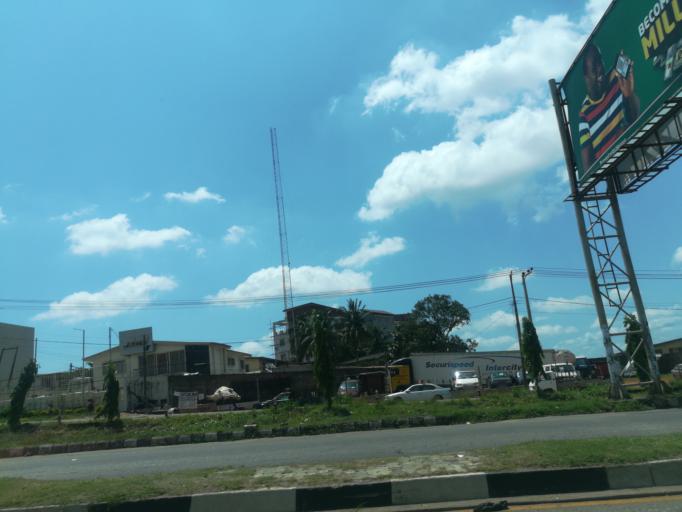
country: NG
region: Oyo
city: Ibadan
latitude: 7.3644
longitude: 3.8635
